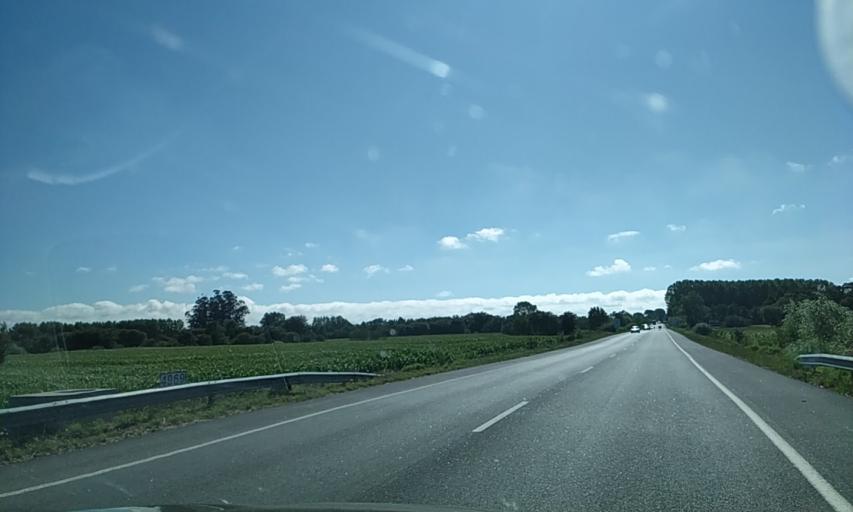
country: PT
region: Aveiro
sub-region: Aveiro
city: Eixo
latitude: 40.6832
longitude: -8.5714
